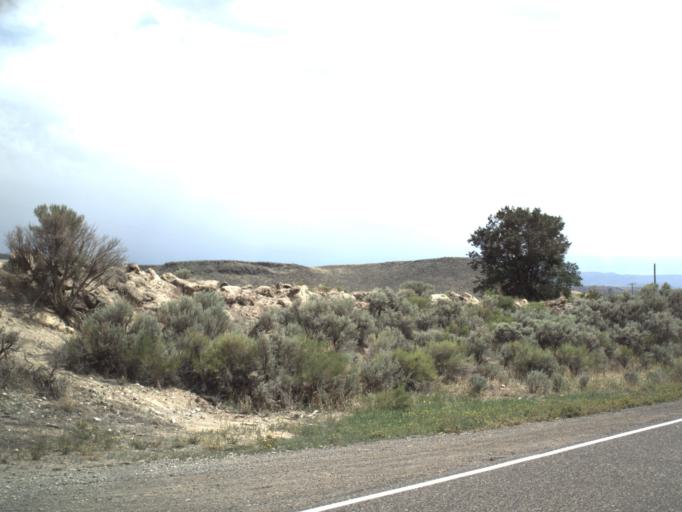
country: US
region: Utah
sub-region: Piute County
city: Junction
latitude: 38.1526
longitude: -112.0021
